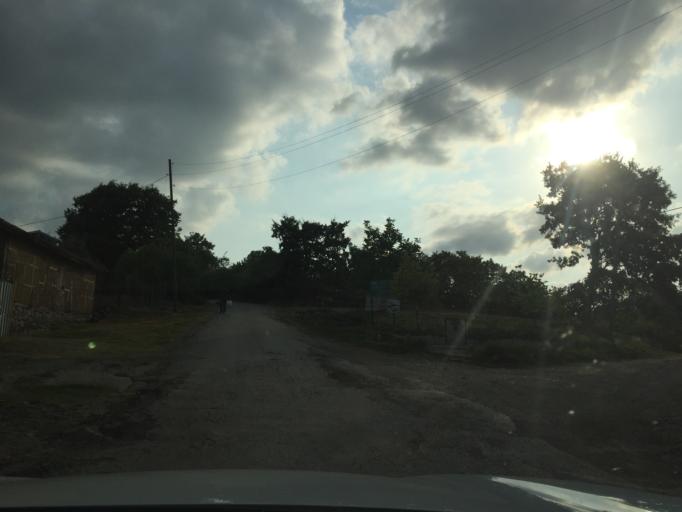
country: TR
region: Balikesir
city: Gonen
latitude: 40.0473
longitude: 27.5802
